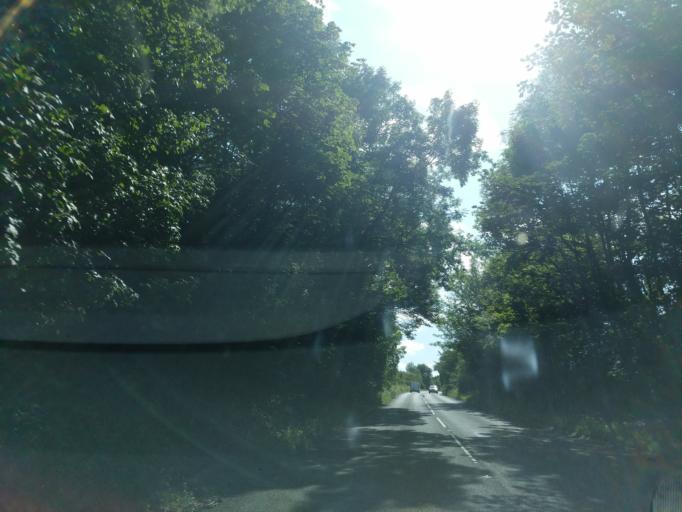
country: GB
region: England
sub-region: Staffordshire
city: Rugeley
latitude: 52.8085
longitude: -1.9225
